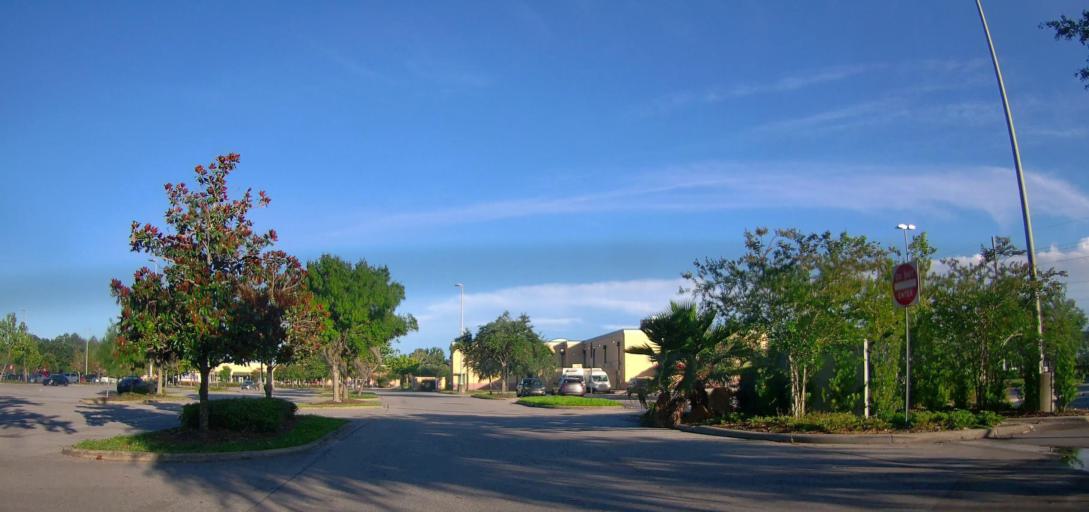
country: US
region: Florida
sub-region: Orange County
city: Hunters Creek
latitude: 28.3316
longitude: -81.4731
